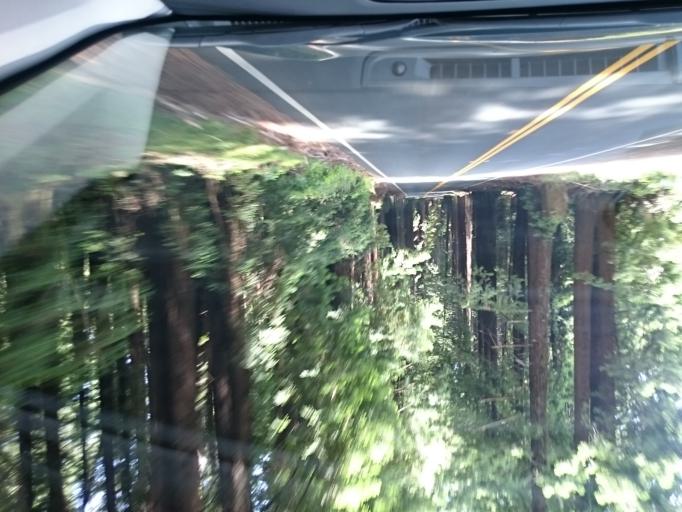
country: US
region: California
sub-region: Mendocino County
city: Boonville
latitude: 39.1648
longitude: -123.6401
